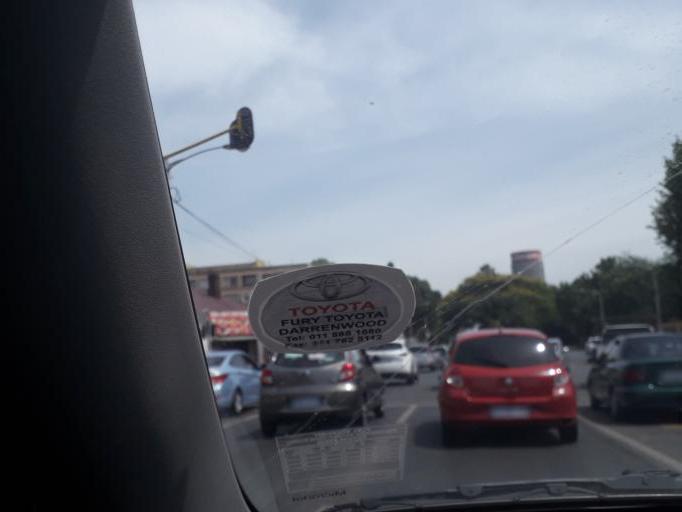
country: ZA
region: Gauteng
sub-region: City of Johannesburg Metropolitan Municipality
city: Johannesburg
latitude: -26.1792
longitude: 28.0582
